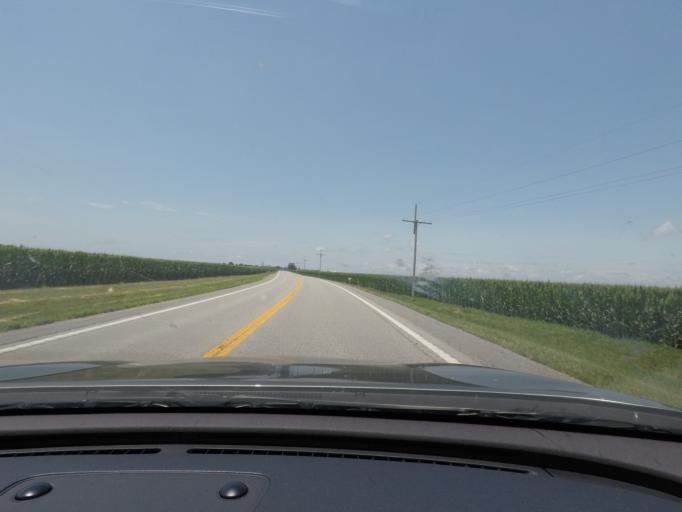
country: US
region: Missouri
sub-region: Saline County
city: Marshall
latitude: 39.1915
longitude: -93.3184
